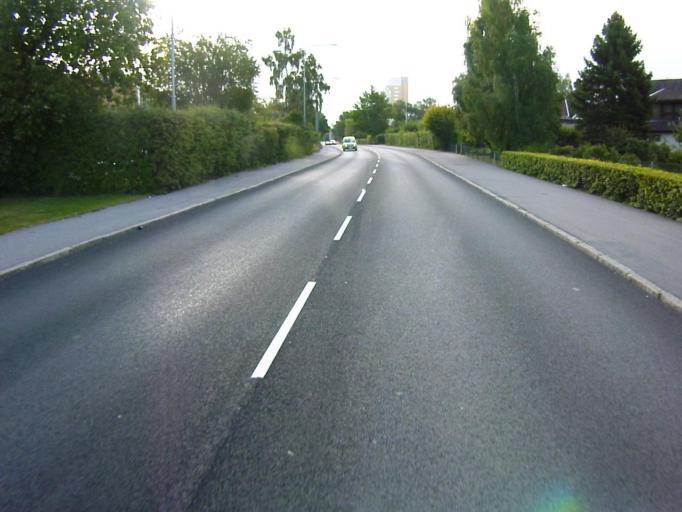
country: SE
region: Soedermanland
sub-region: Eskilstuna Kommun
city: Eskilstuna
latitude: 59.3742
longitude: 16.4865
